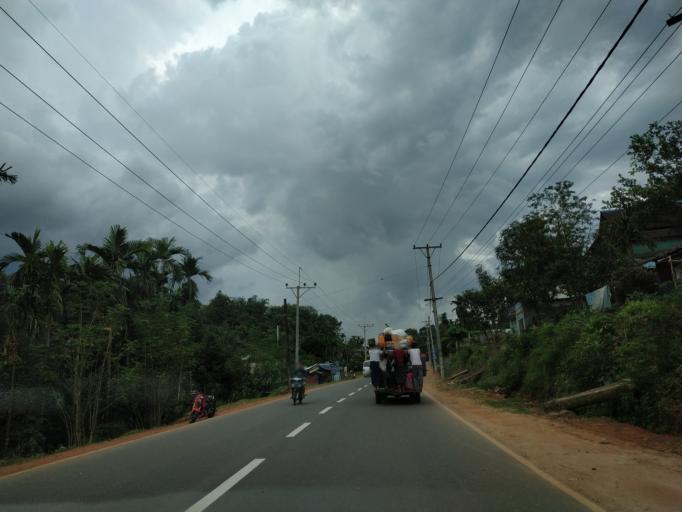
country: MM
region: Tanintharyi
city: Dawei
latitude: 13.9720
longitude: 98.2402
